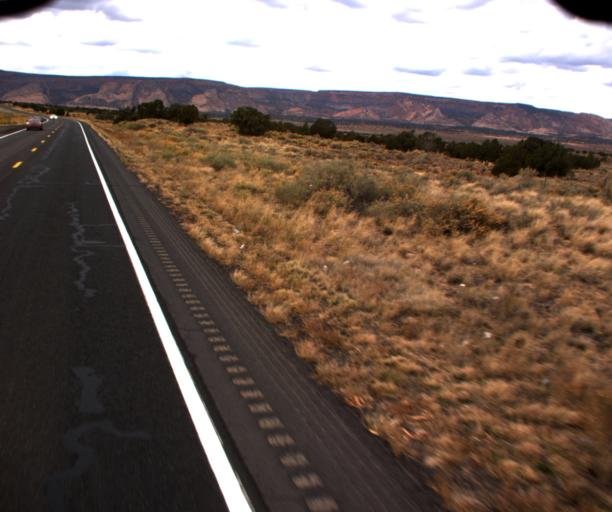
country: US
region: Arizona
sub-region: Navajo County
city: Kayenta
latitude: 36.6986
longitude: -110.3332
